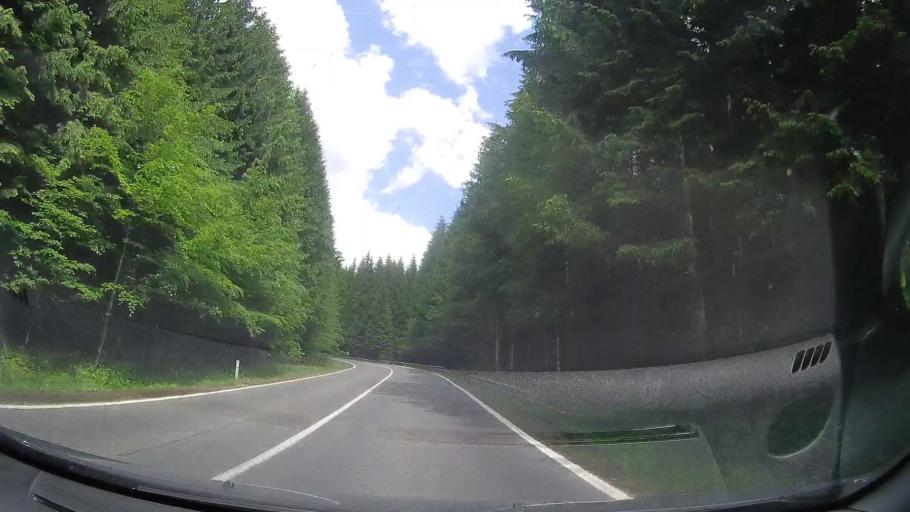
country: RO
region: Brasov
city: Crivina
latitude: 45.4597
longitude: 25.9536
